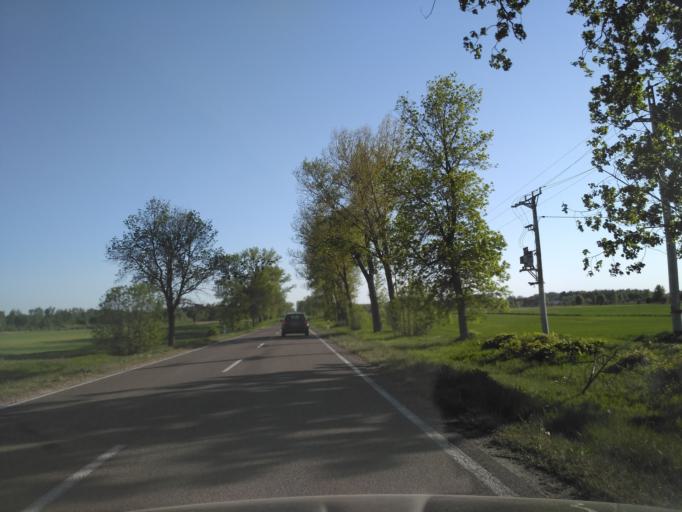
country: PL
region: Lublin Voivodeship
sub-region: Powiat leczynski
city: Cycow
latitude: 51.2190
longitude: 23.0759
